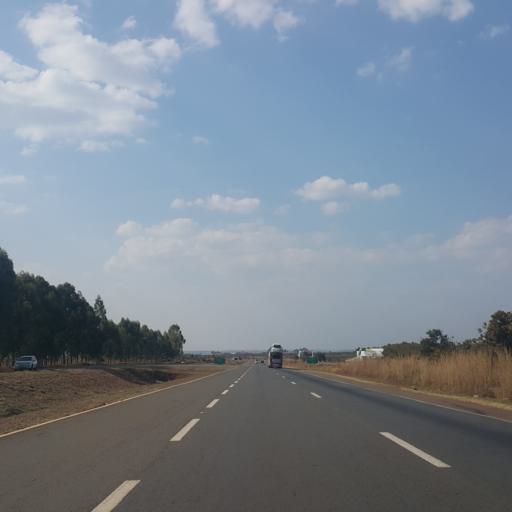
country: BR
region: Goias
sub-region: Abadiania
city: Abadiania
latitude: -16.2110
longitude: -48.7439
